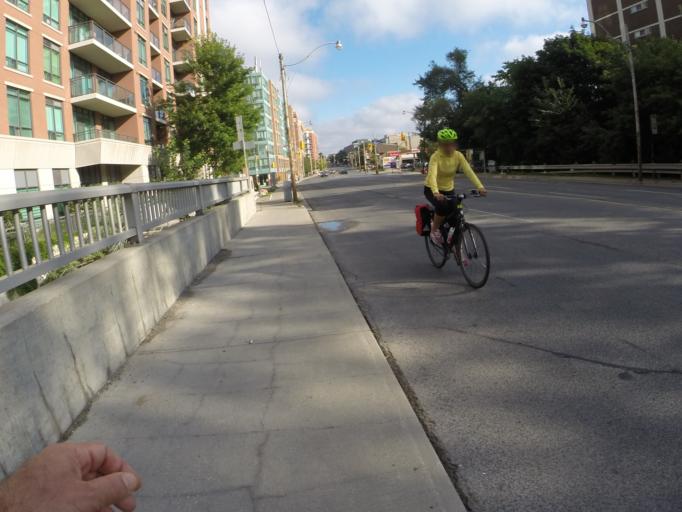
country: CA
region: Ontario
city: Toronto
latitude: 43.6973
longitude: -79.3862
